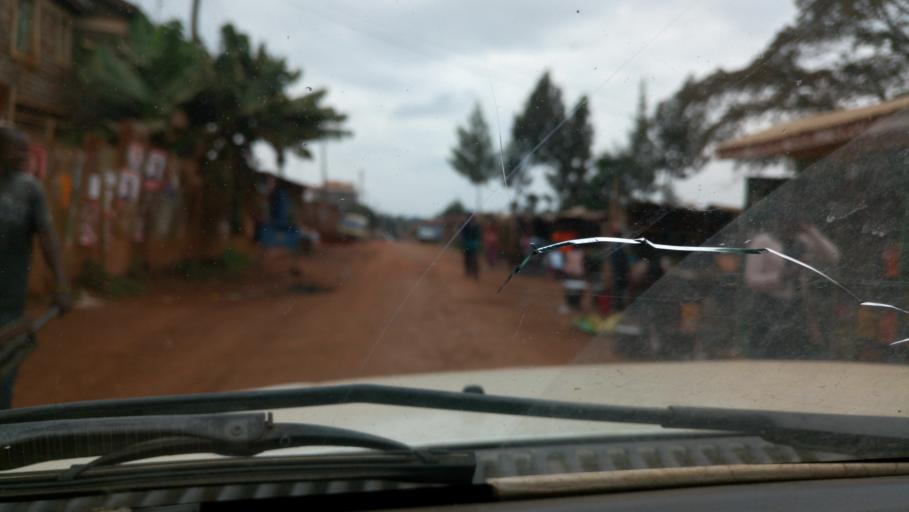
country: KE
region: Kiambu
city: Kikuyu
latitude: -1.2666
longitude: 36.7187
